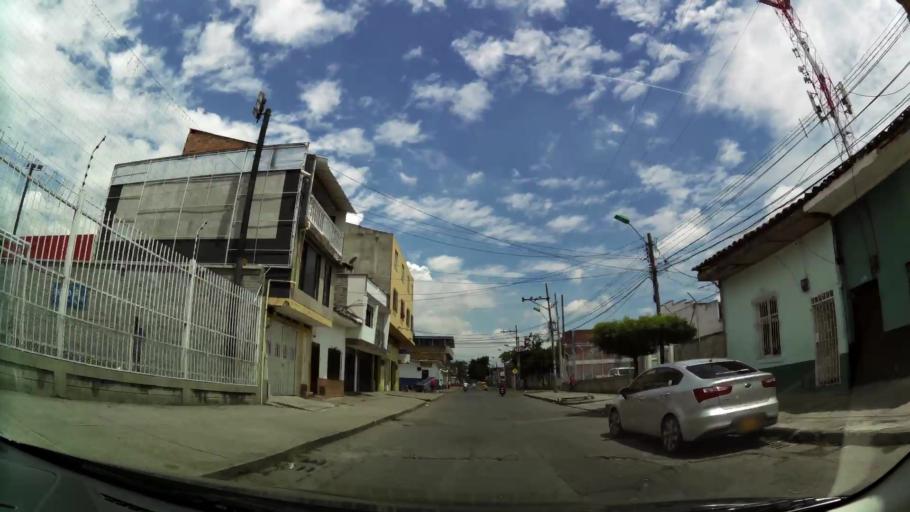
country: CO
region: Valle del Cauca
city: Cali
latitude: 3.4470
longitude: -76.5197
